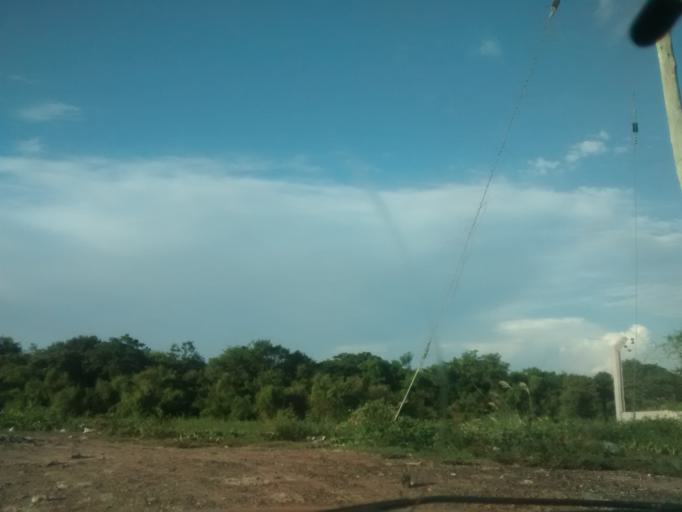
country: AR
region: Chaco
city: Resistencia
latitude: -27.4296
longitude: -58.9911
